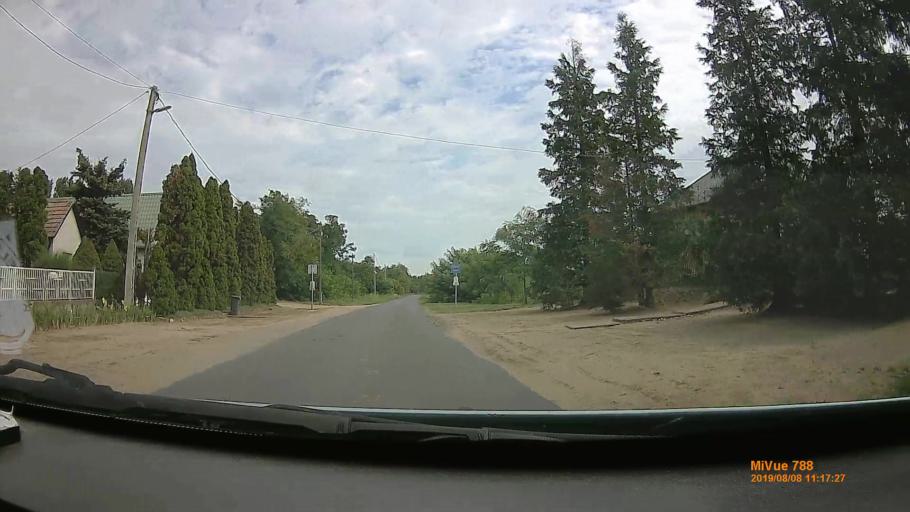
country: HU
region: Szabolcs-Szatmar-Bereg
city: Balkany
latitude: 47.7305
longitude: 21.8323
